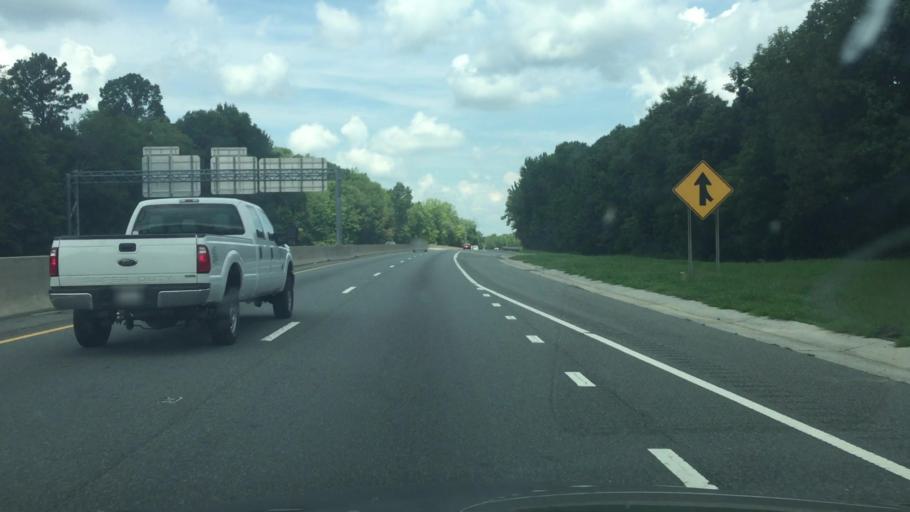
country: US
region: North Carolina
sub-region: Randolph County
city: Asheboro
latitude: 35.6888
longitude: -79.8312
